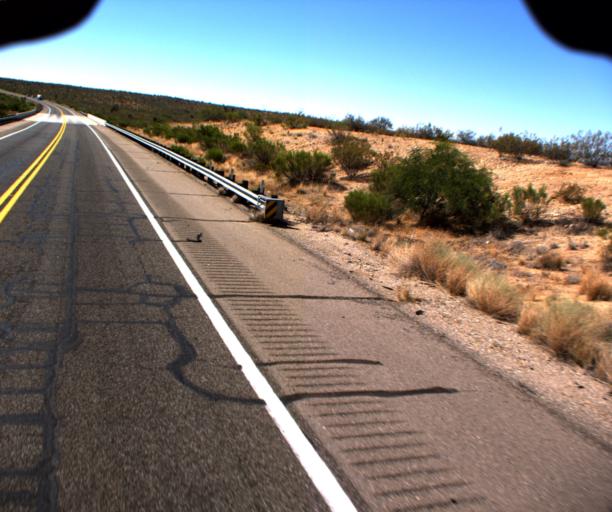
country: US
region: Arizona
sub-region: Yavapai County
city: Congress
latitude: 34.2069
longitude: -113.0645
